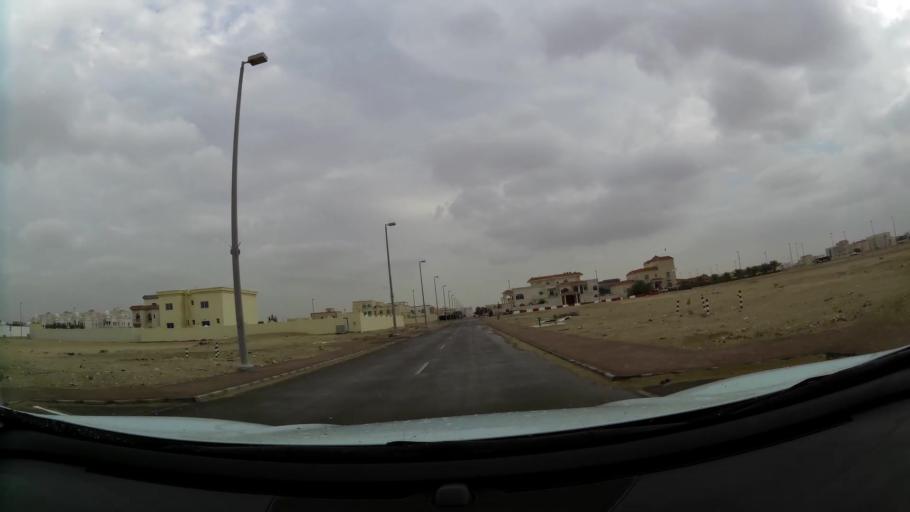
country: AE
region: Abu Dhabi
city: Abu Dhabi
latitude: 24.3558
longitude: 54.6180
